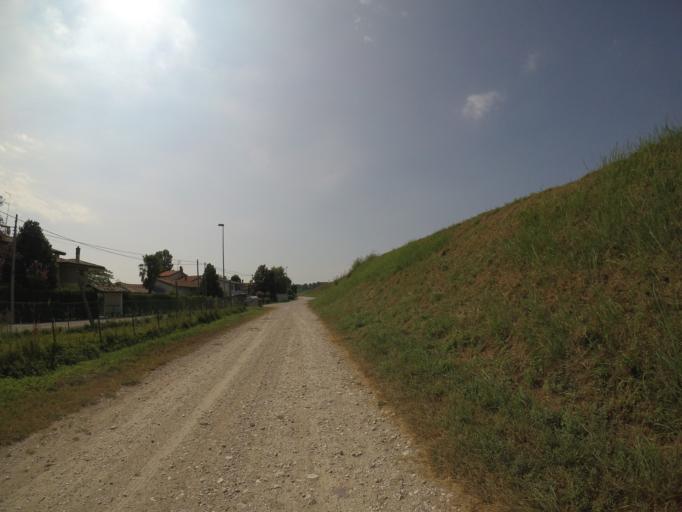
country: IT
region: Friuli Venezia Giulia
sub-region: Provincia di Udine
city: Pertegada
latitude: 45.7122
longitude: 13.0414
